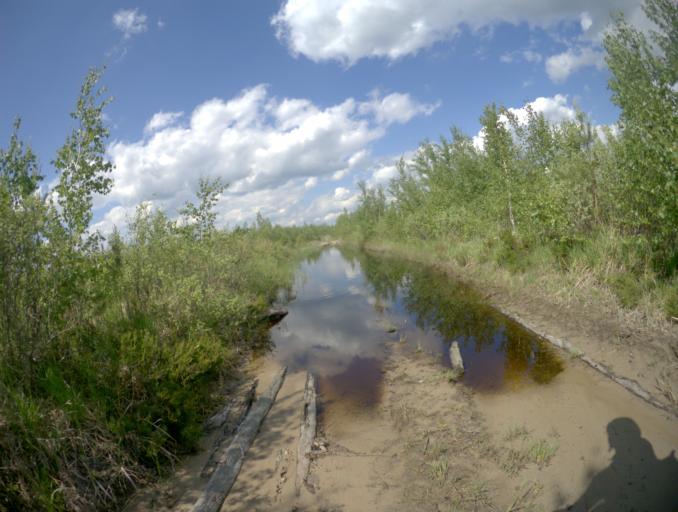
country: RU
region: Vladimir
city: Velikodvorskiy
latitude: 55.2916
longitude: 40.8933
